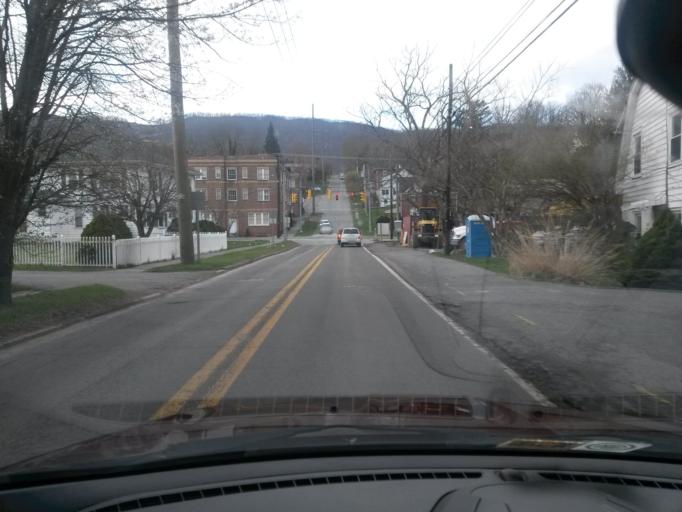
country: US
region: West Virginia
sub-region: Mercer County
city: Bluefield
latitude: 37.2510
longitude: -81.2317
